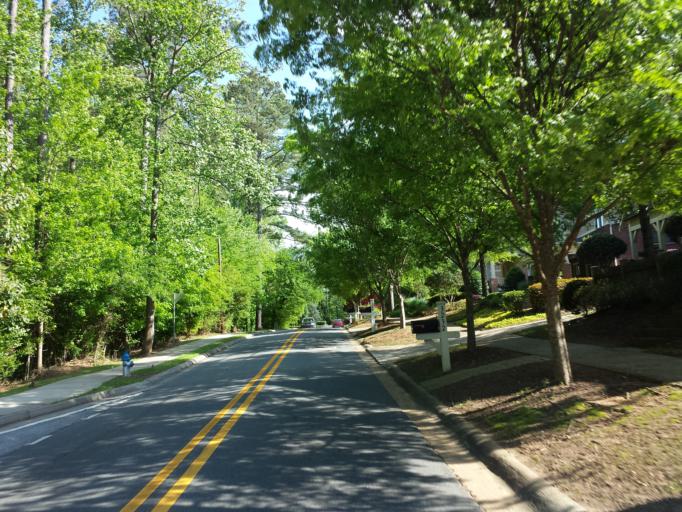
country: US
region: Georgia
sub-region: Cobb County
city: Smyrna
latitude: 33.8749
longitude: -84.5191
